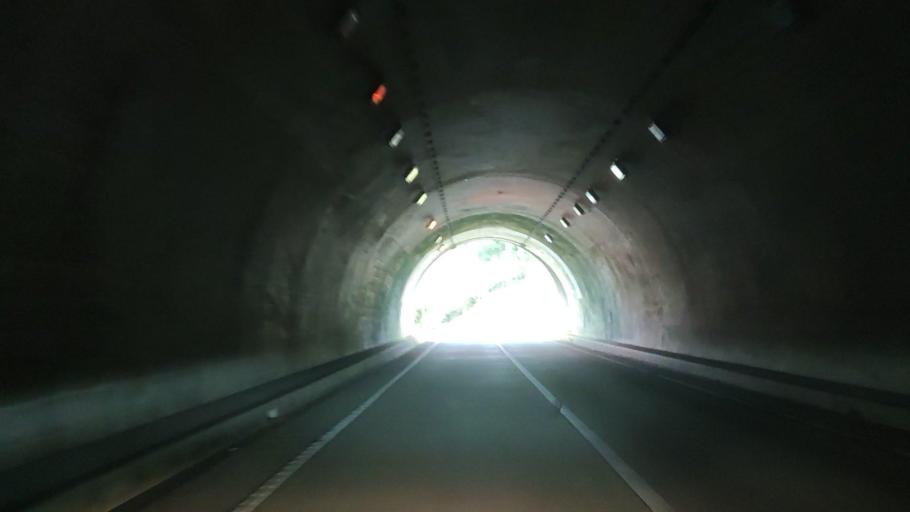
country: JP
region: Shizuoka
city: Heda
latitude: 34.9114
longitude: 138.8480
